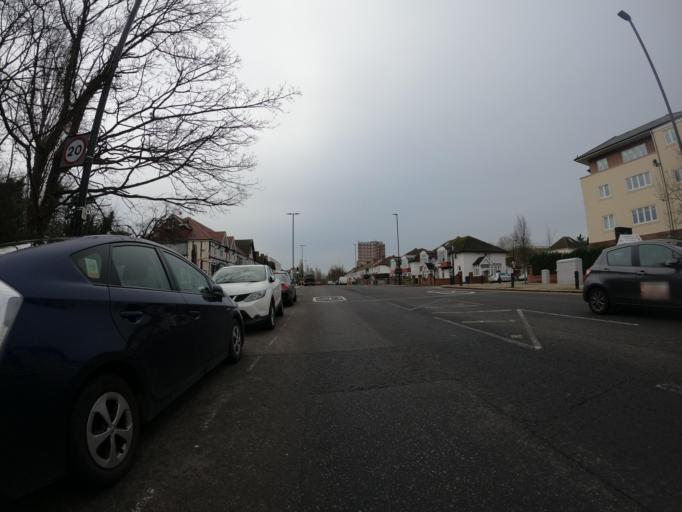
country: GB
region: England
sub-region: Greater London
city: Greenford
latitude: 51.5196
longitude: -0.3545
